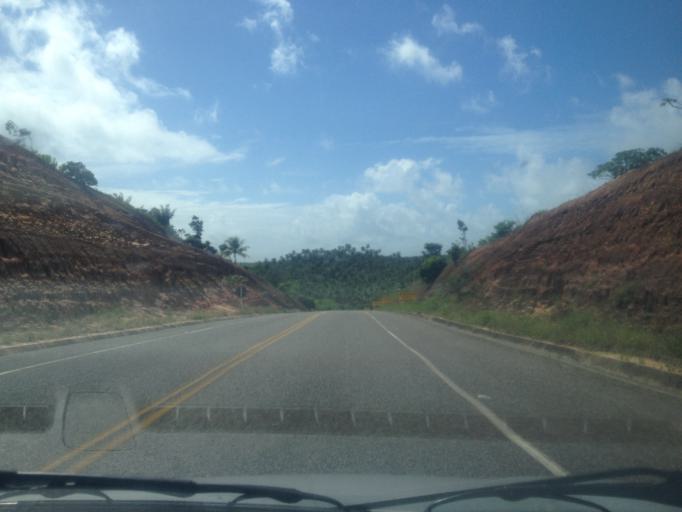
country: BR
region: Bahia
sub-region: Conde
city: Conde
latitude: -11.9718
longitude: -37.6747
